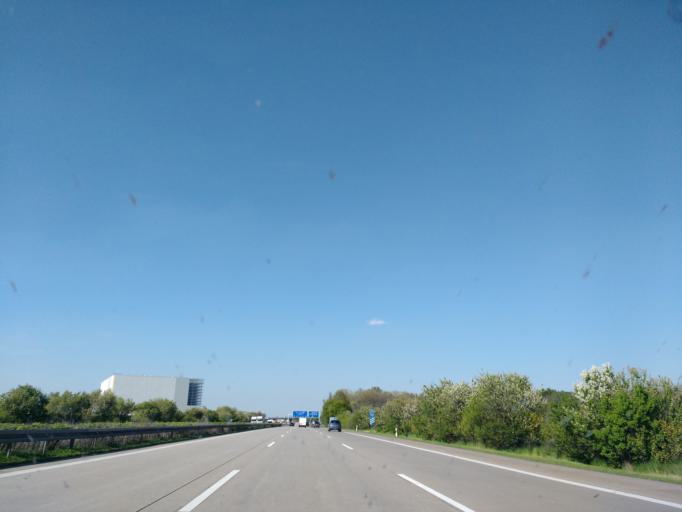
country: DE
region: Saxony-Anhalt
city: Gunthersdorf
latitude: 51.3378
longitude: 12.1809
